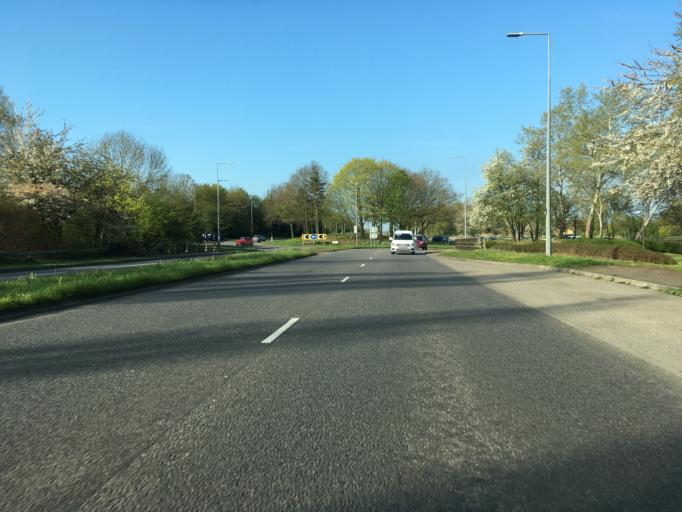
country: GB
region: England
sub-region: Milton Keynes
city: Bradwell
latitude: 52.0543
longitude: -0.7840
